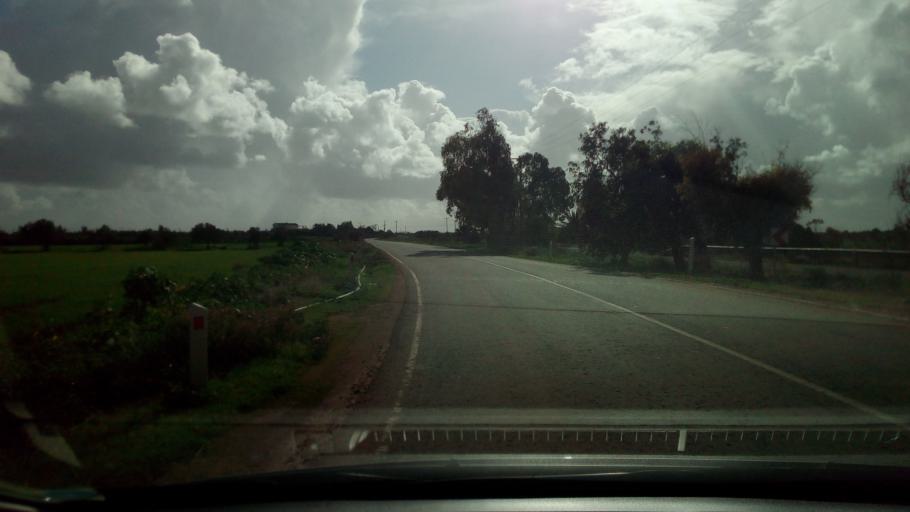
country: CY
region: Ammochostos
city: Avgorou
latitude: 35.0526
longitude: 33.8147
